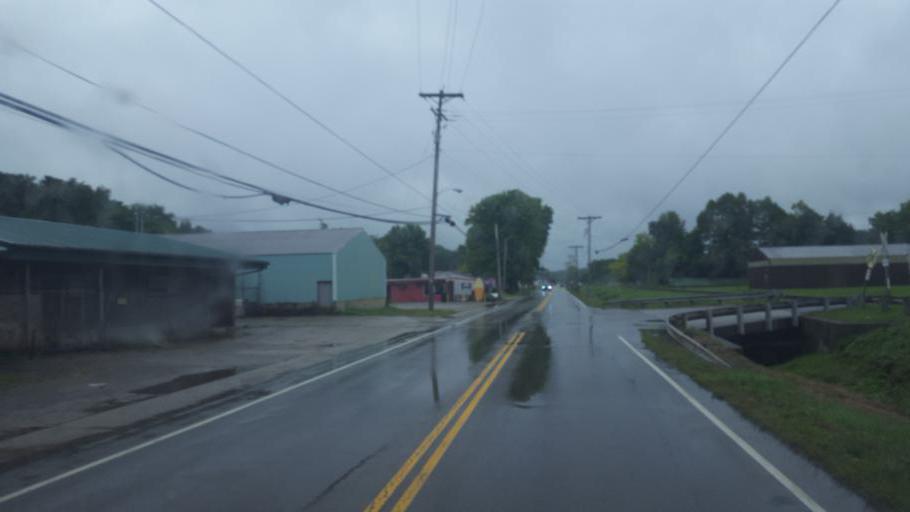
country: US
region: Ohio
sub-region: Jackson County
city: Oak Hill
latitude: 38.8918
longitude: -82.5739
